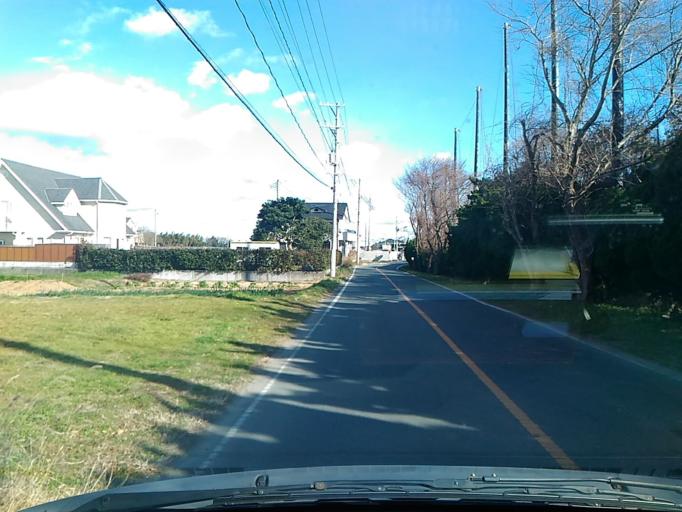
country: JP
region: Fukushima
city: Iwaki
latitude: 36.9196
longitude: 140.8476
